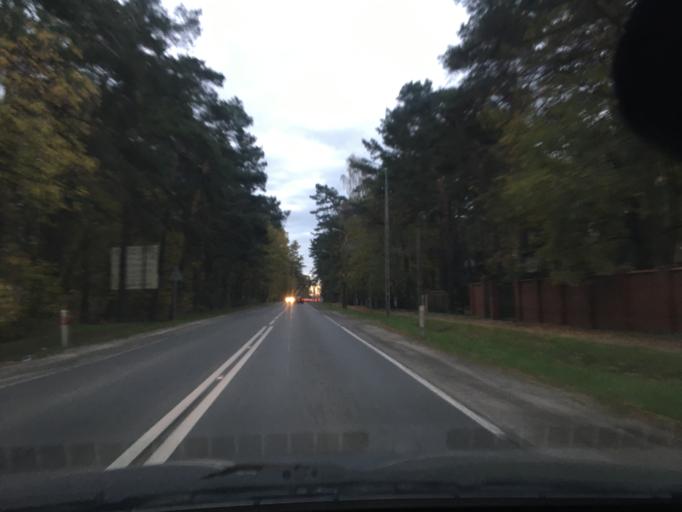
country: PL
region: Masovian Voivodeship
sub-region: Powiat piaseczynski
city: Lesznowola
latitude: 52.0980
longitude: 20.9116
